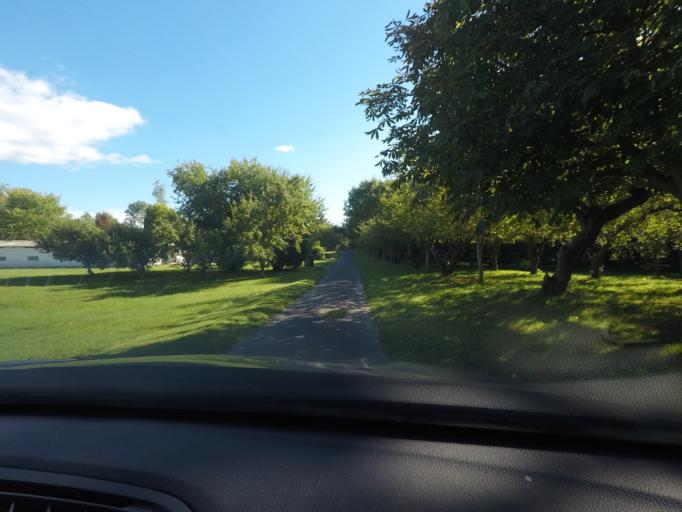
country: DK
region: Zealand
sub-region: Guldborgsund Kommune
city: Sakskobing
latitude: 54.9700
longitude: 11.5330
